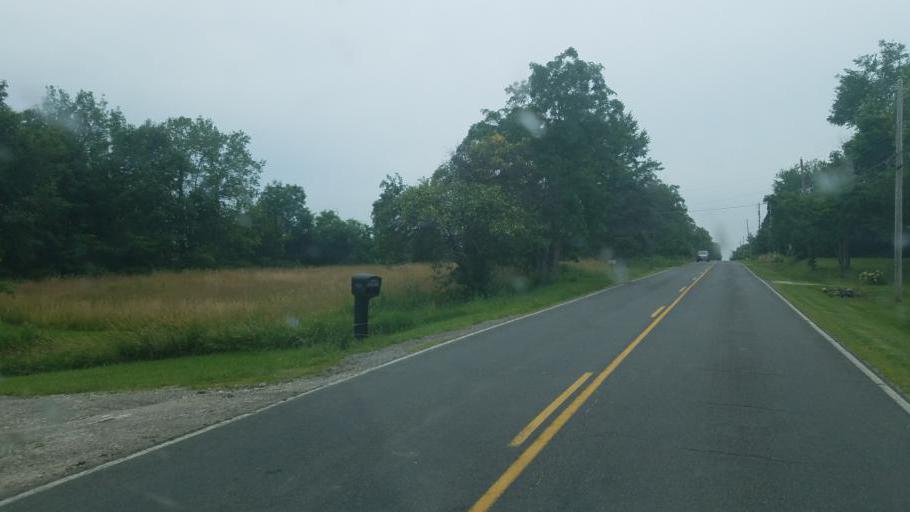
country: US
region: Ohio
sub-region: Portage County
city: Ravenna
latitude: 41.0994
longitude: -81.1288
